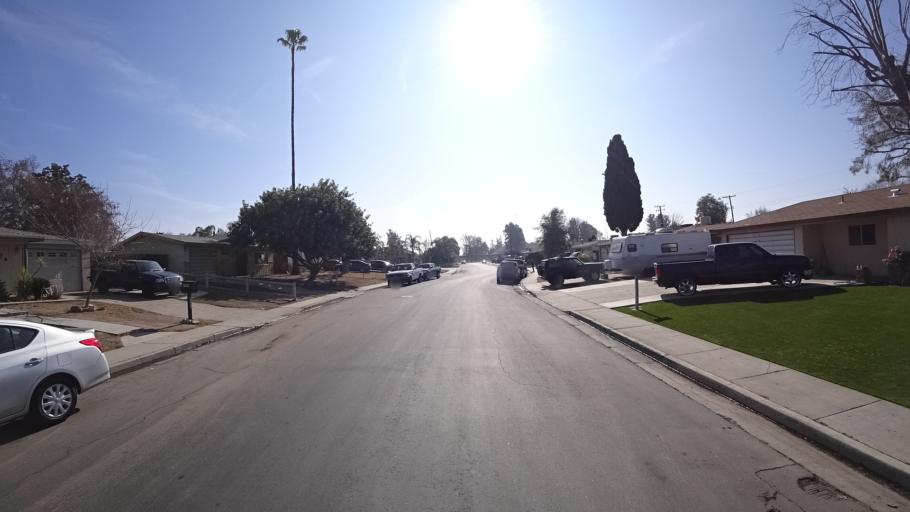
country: US
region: California
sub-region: Kern County
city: Bakersfield
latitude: 35.3340
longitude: -119.0505
